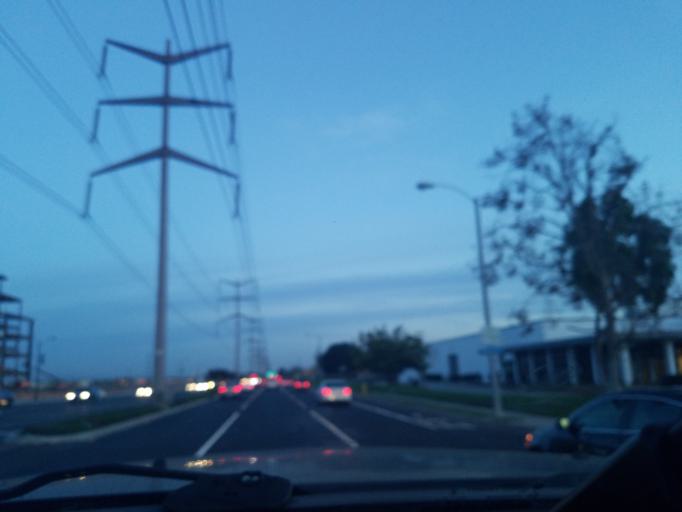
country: US
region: California
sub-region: Orange County
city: Irvine
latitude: 33.7036
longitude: -117.8405
